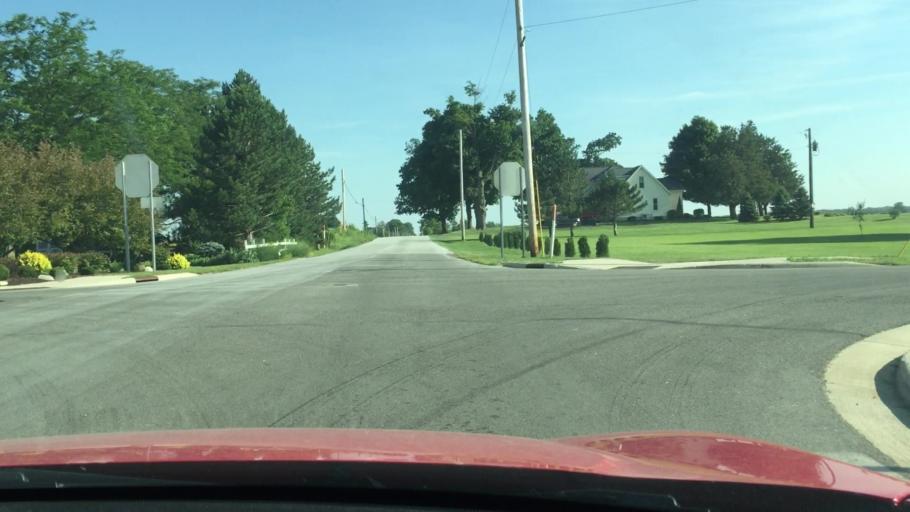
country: US
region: Ohio
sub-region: Hardin County
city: Ada
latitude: 40.7620
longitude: -83.8424
